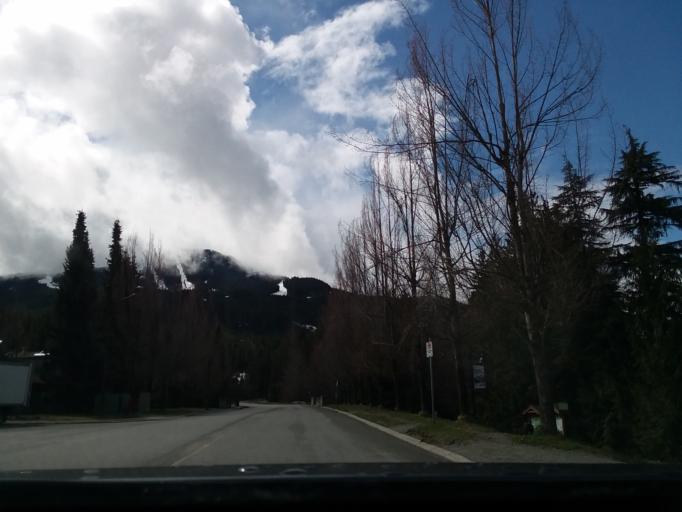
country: CA
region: British Columbia
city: Whistler
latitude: 50.1162
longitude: -122.9489
